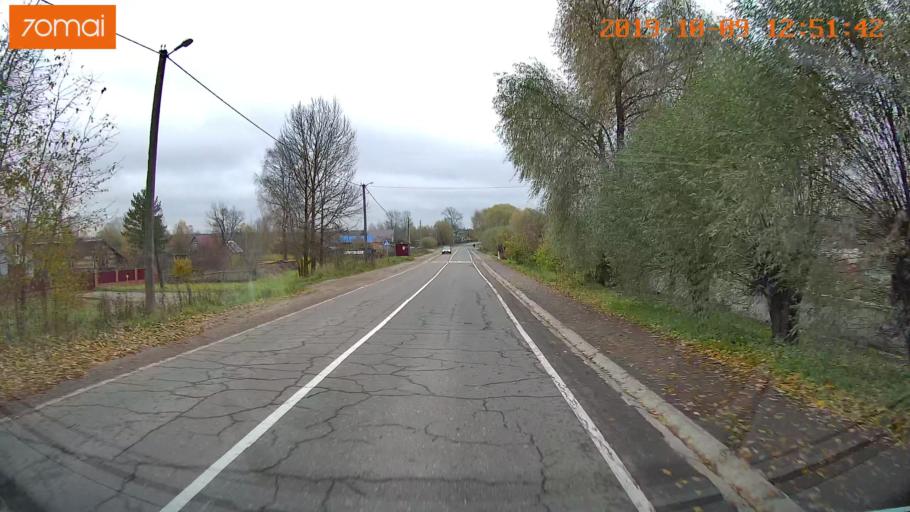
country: RU
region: Jaroslavl
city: Prechistoye
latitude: 58.4181
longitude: 40.3454
